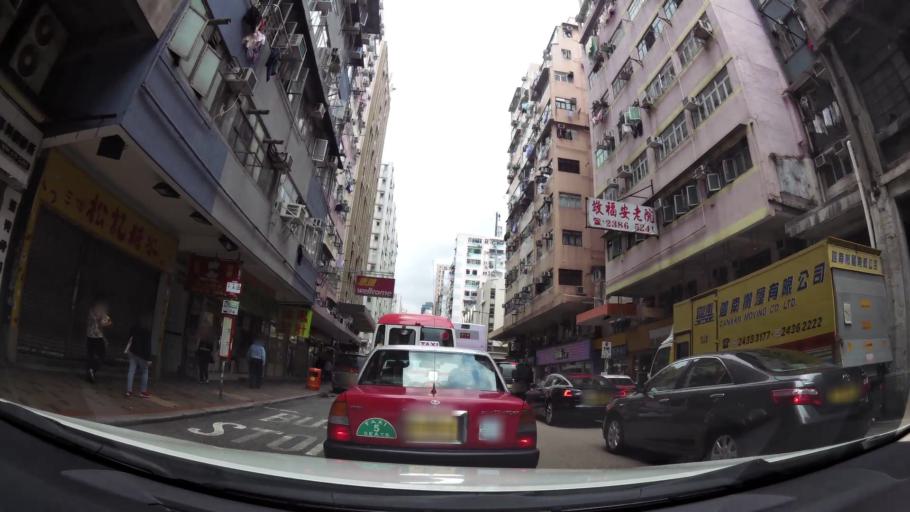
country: HK
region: Sham Shui Po
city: Sham Shui Po
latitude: 22.3342
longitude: 114.1608
